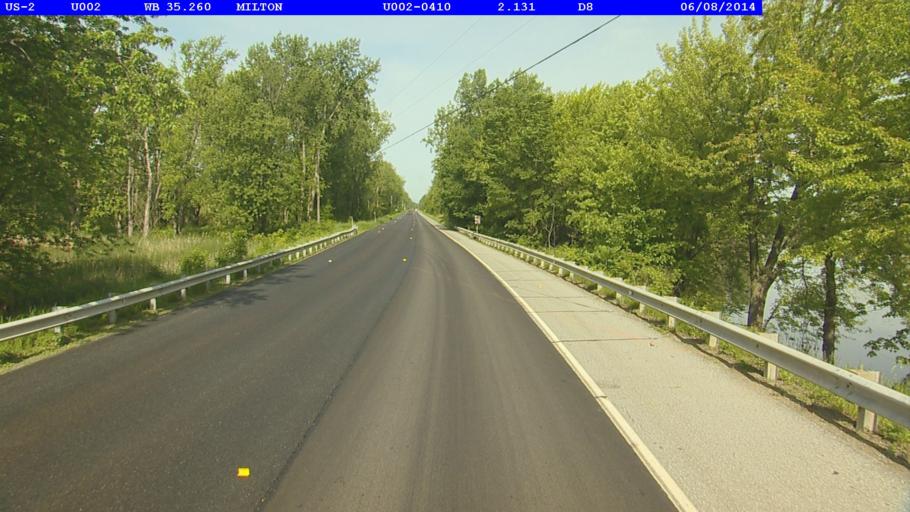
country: US
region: Vermont
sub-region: Chittenden County
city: Colchester
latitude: 44.6234
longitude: -73.2150
